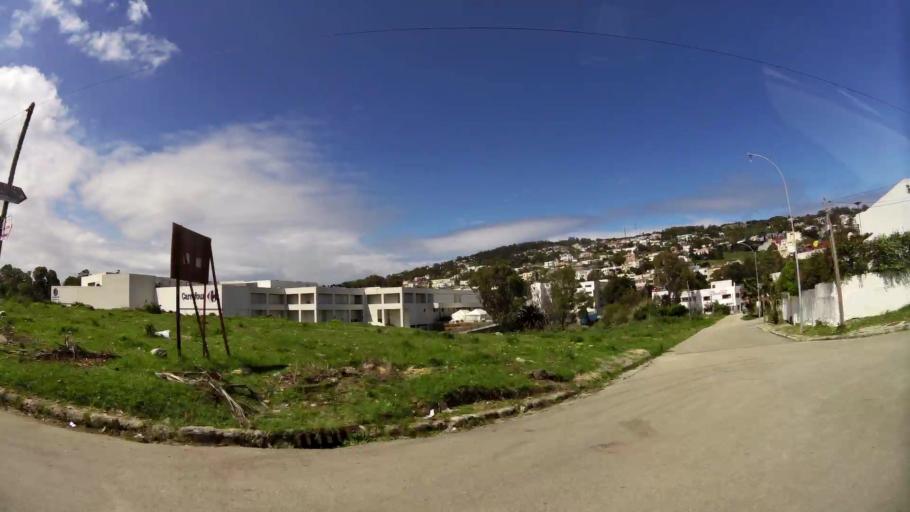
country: MA
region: Tanger-Tetouan
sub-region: Tanger-Assilah
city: Tangier
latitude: 35.7815
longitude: -5.8383
